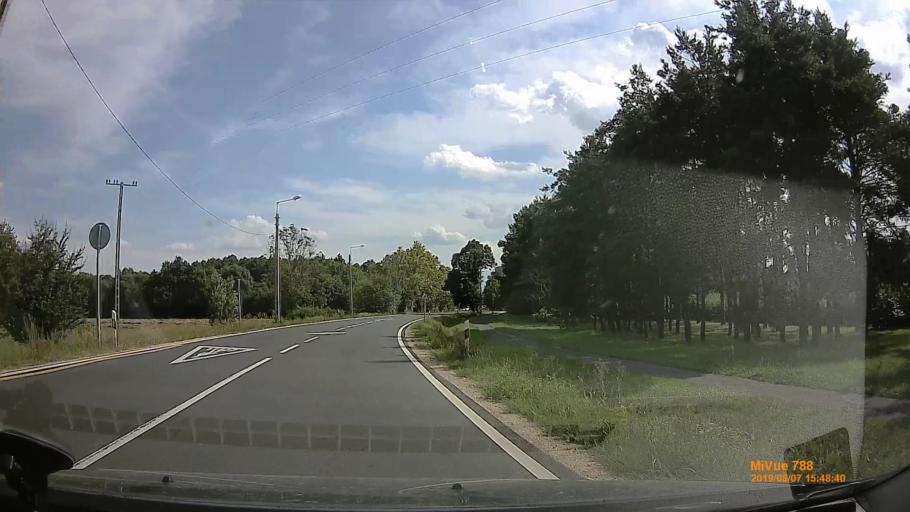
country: HU
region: Vas
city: Jak
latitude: 47.1591
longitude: 16.6383
